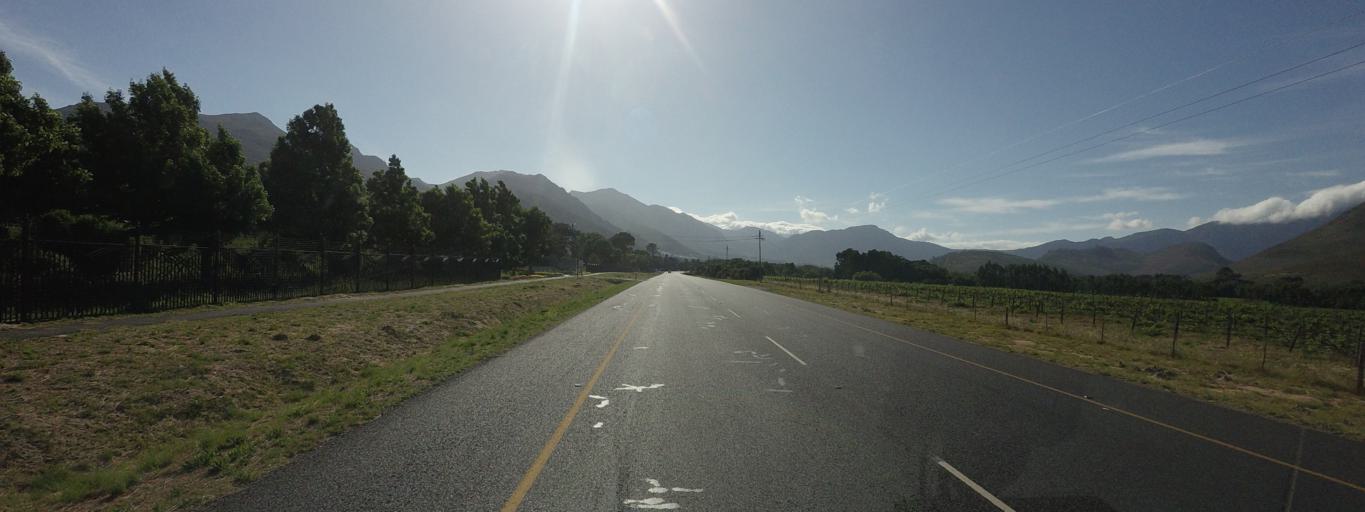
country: ZA
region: Western Cape
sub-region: Cape Winelands District Municipality
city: Paarl
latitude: -33.8797
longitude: 19.0578
